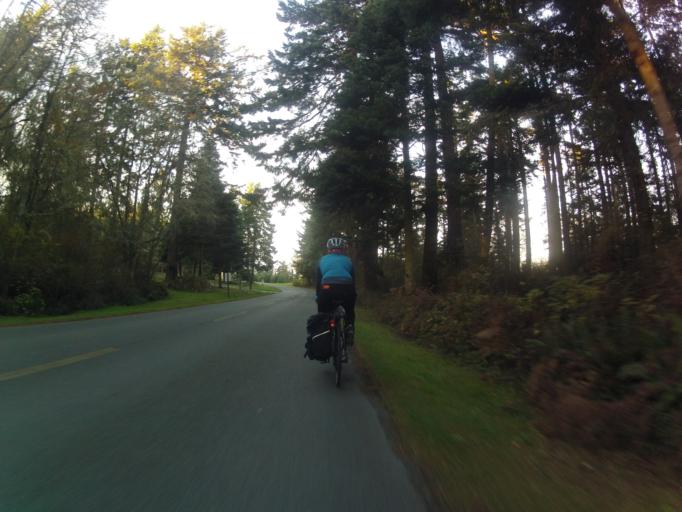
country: US
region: Washington
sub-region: Island County
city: Coupeville
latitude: 48.1598
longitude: -122.6763
